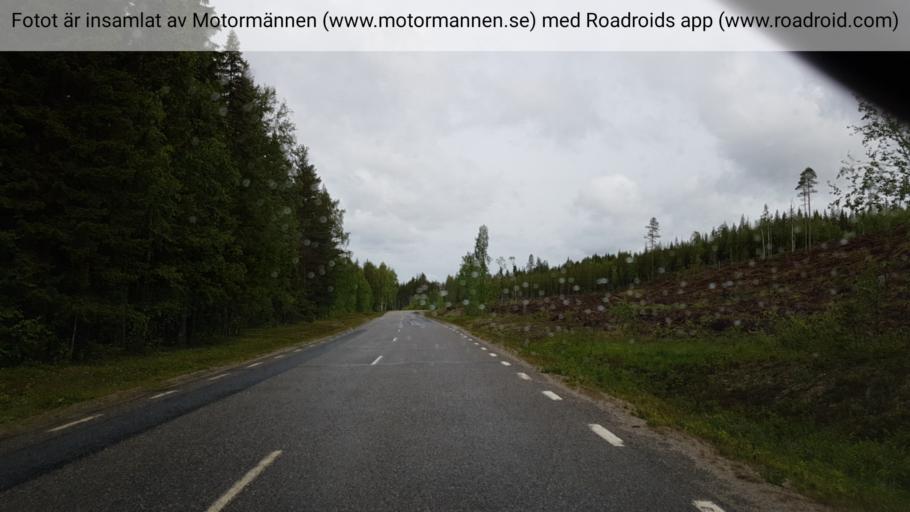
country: SE
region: Vaesterbotten
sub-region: Norsjo Kommun
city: Norsjoe
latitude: 64.6204
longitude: 19.2880
